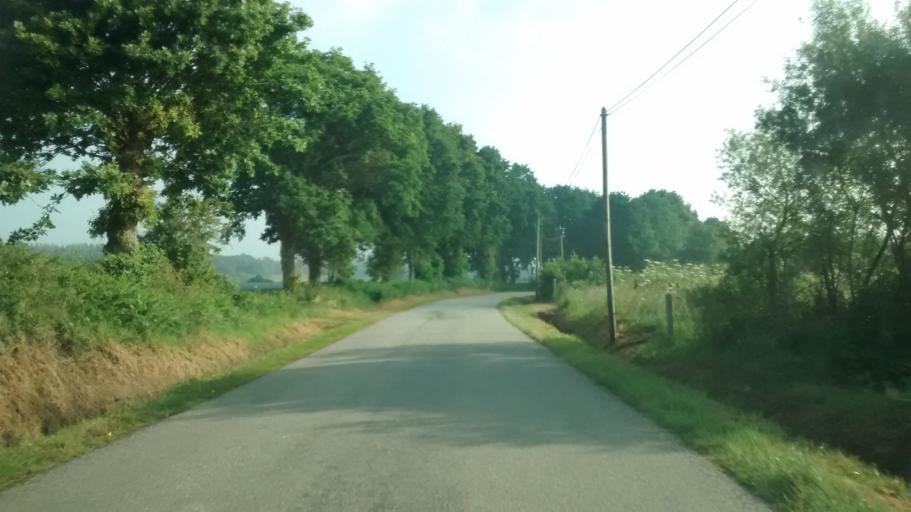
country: FR
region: Brittany
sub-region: Departement du Morbihan
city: Ruffiac
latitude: 47.8339
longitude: -2.2768
